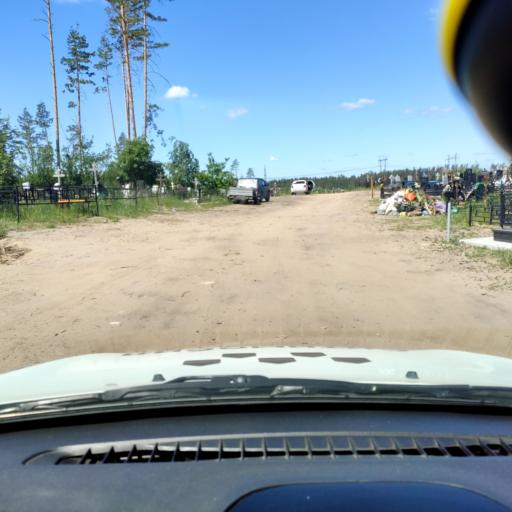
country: RU
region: Samara
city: Zhigulevsk
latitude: 53.5345
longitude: 49.5536
